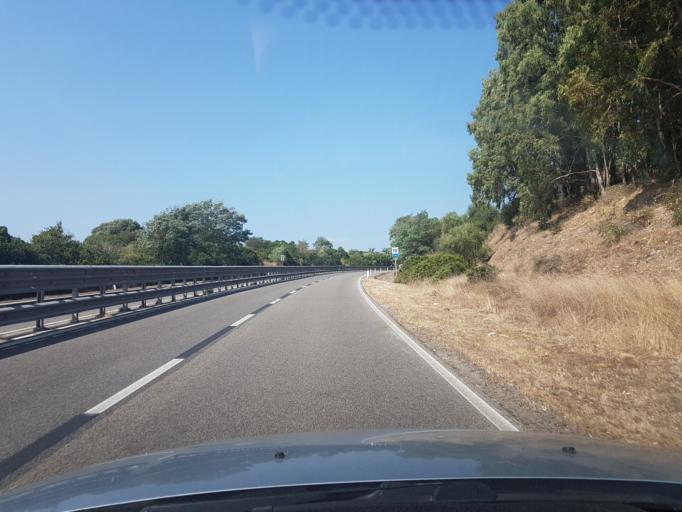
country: IT
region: Sardinia
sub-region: Provincia di Oristano
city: Soddi
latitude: 40.1494
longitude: 8.8952
